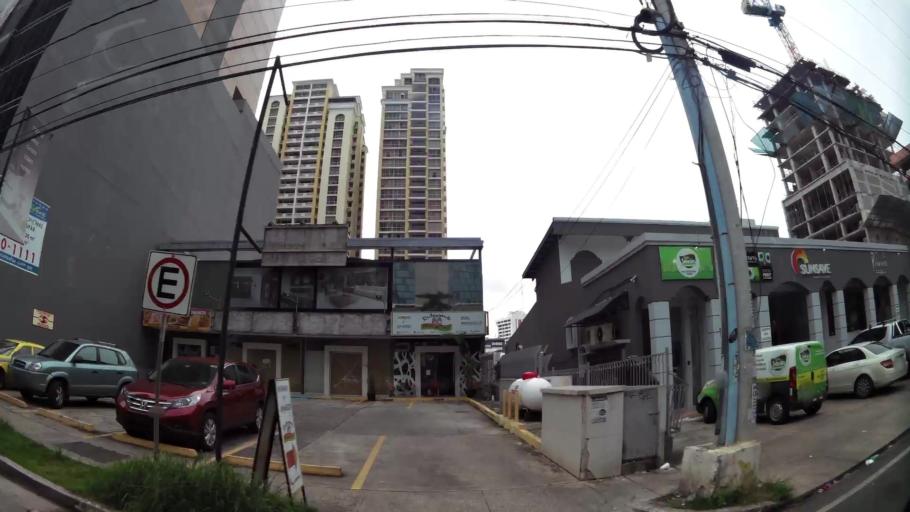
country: PA
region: Panama
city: Panama
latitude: 8.9868
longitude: -79.5216
